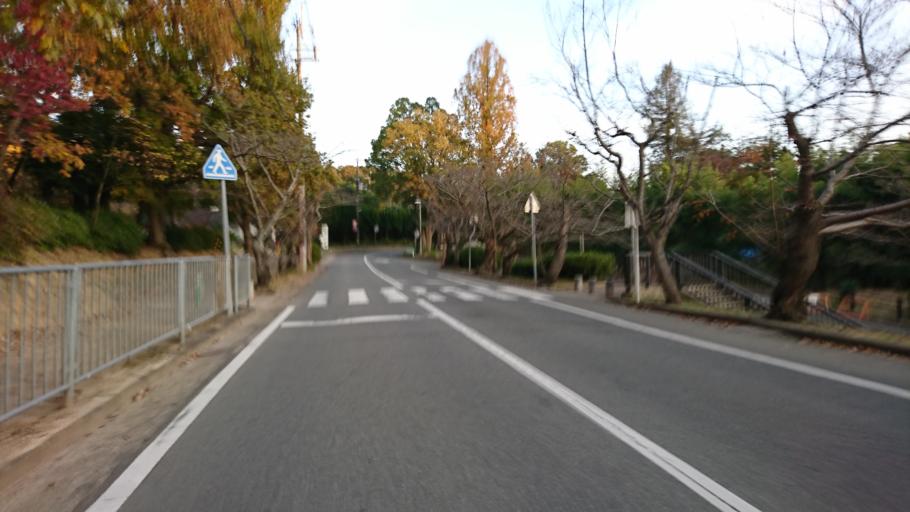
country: JP
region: Hyogo
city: Kakogawacho-honmachi
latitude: 34.7772
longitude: 134.8621
